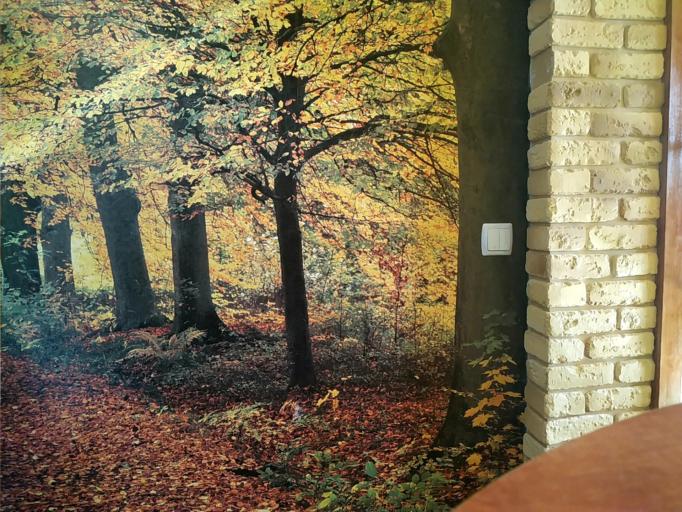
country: RU
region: Jaroslavl
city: Kukoboy
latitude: 58.8235
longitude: 39.7617
